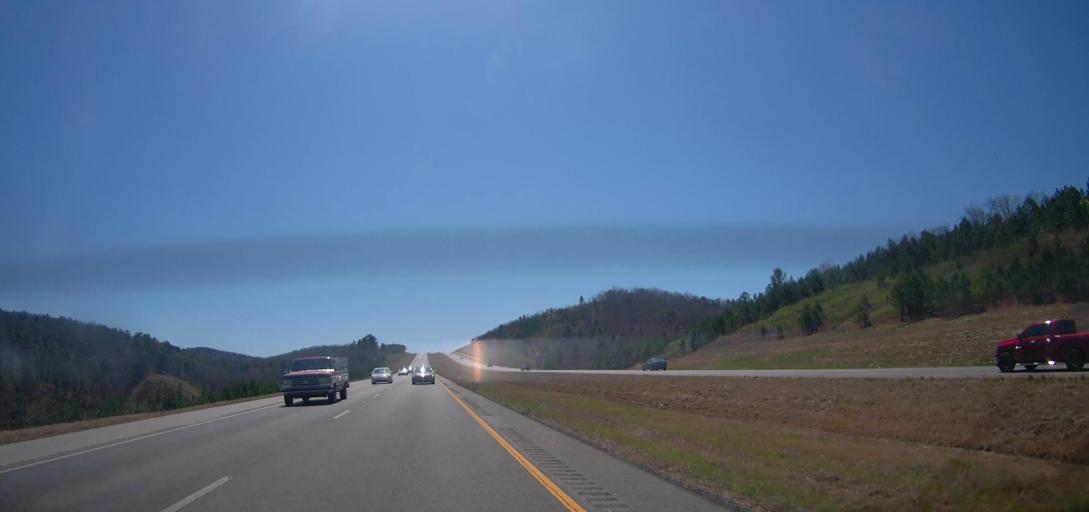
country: US
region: Alabama
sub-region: Calhoun County
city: Saks
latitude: 33.6949
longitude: -85.8067
